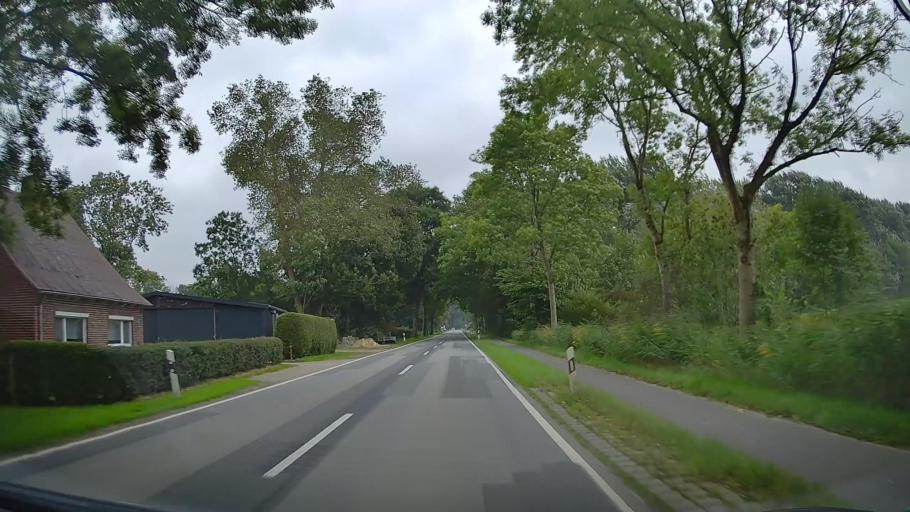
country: DE
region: Lower Saxony
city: Geversdorf
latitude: 53.8198
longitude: 9.0972
